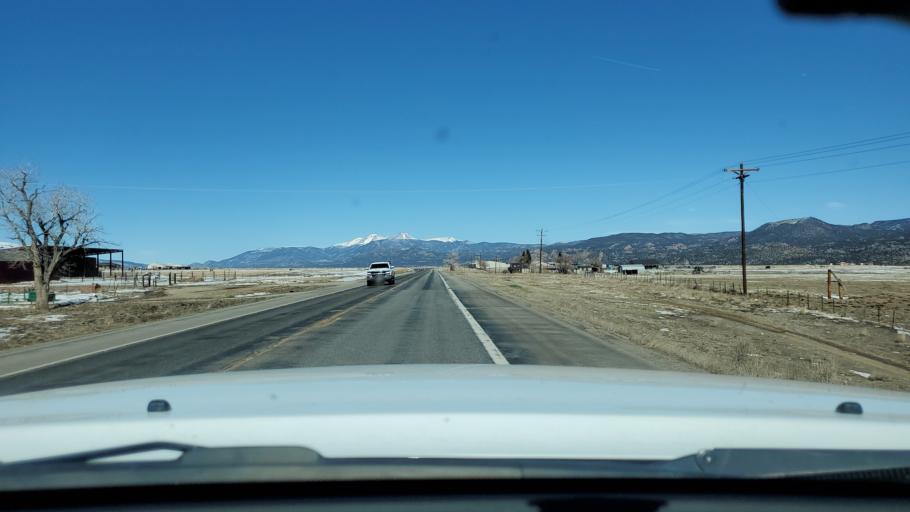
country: US
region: Colorado
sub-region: Chaffee County
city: Buena Vista
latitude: 38.6966
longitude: -106.0897
